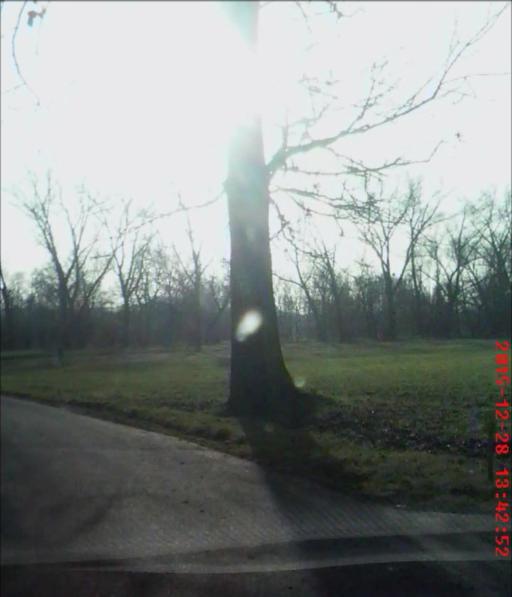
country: DE
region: Thuringia
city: Eberstedt
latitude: 51.0732
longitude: 11.5791
